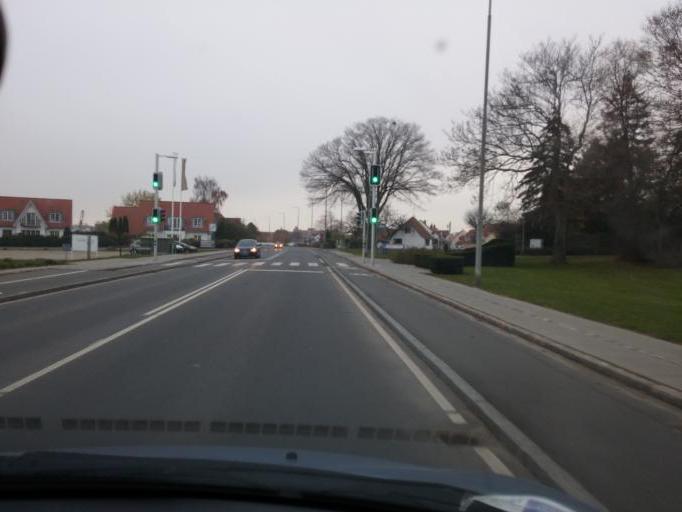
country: DK
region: South Denmark
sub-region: Kerteminde Kommune
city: Kerteminde
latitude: 55.4553
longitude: 10.6623
